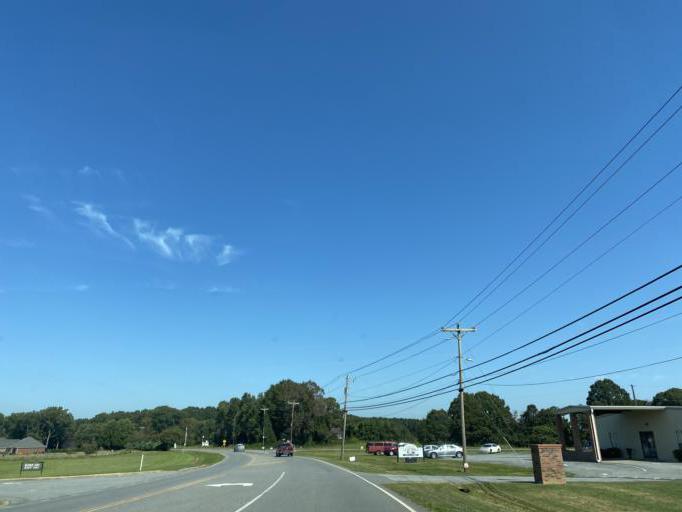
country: US
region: North Carolina
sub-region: Cleveland County
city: Boiling Springs
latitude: 35.2762
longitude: -81.6653
